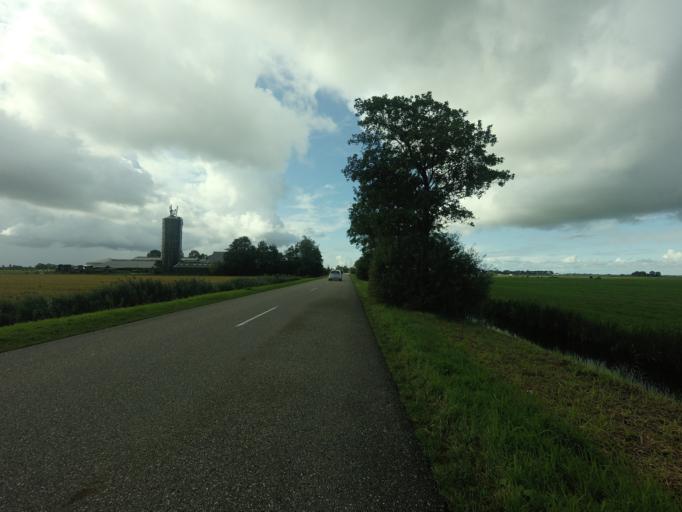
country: NL
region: Friesland
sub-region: Gemeente Boarnsterhim
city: Warten
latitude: 53.1551
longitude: 5.9117
